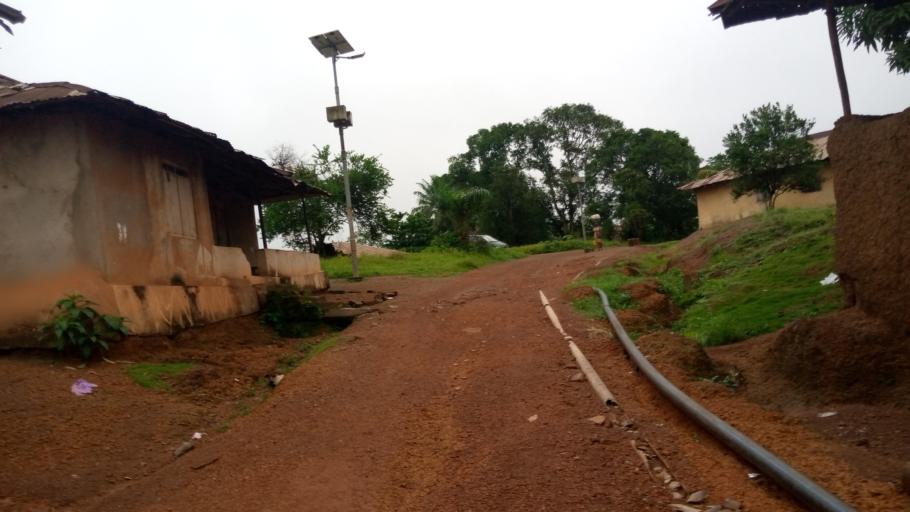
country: SL
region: Southern Province
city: Moyamba
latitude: 8.1616
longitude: -12.4302
